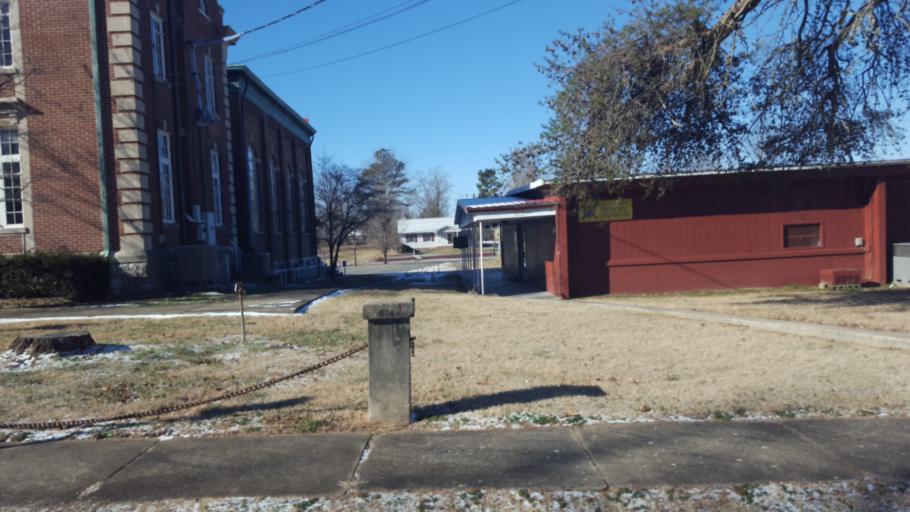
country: US
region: Kentucky
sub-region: Crittenden County
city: Marion
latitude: 37.3343
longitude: -88.0784
